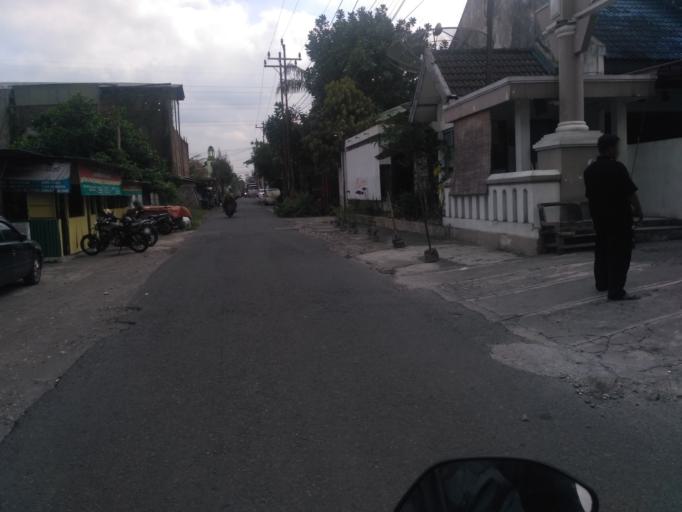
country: ID
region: Daerah Istimewa Yogyakarta
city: Melati
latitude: -7.7564
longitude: 110.3631
